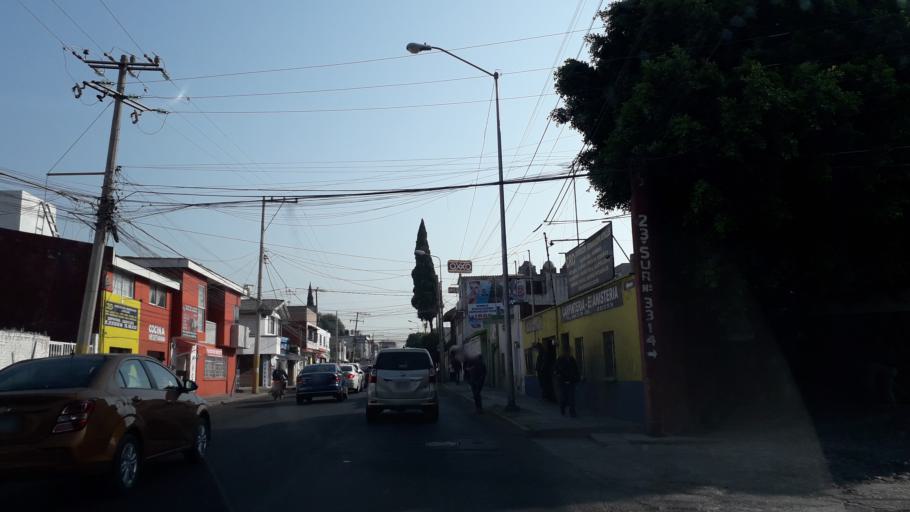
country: MX
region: Puebla
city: Puebla
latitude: 19.0394
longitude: -98.2226
